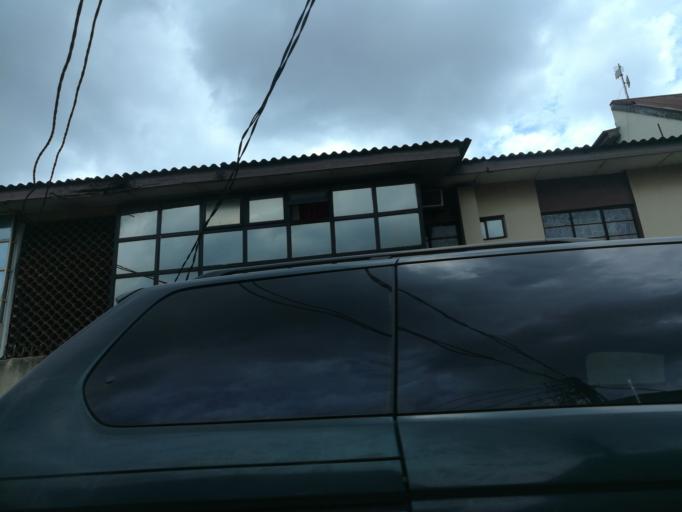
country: NG
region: Lagos
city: Ikeja
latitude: 6.5981
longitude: 3.3476
